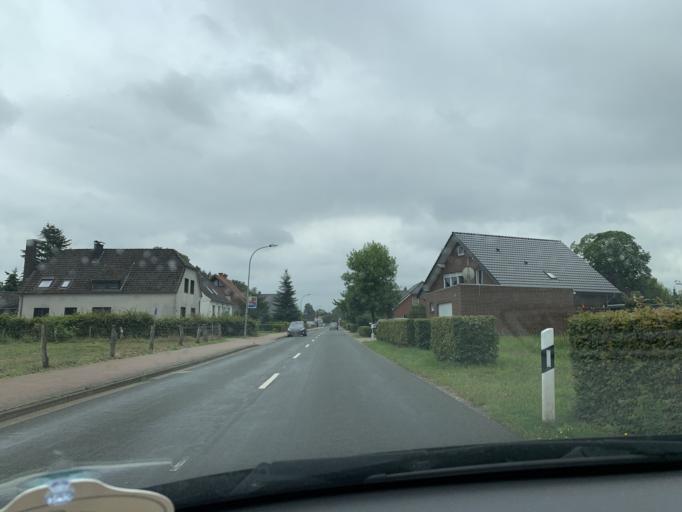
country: DE
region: North Rhine-Westphalia
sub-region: Regierungsbezirk Munster
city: Ostbevern
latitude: 52.1112
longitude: 7.8531
